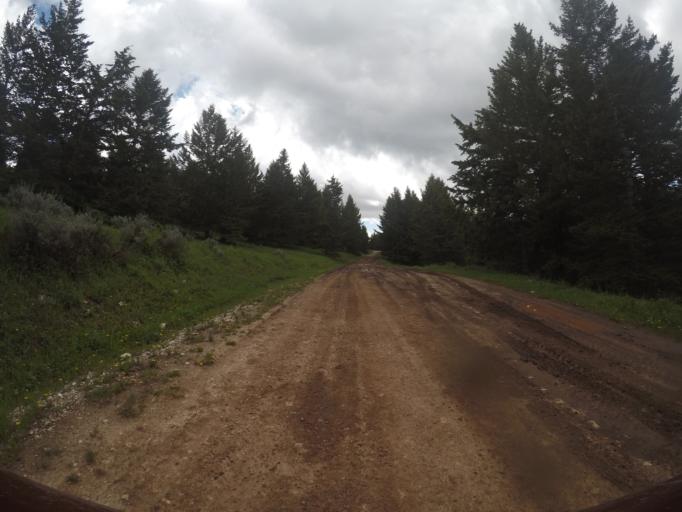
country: US
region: Wyoming
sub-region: Big Horn County
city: Lovell
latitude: 45.1752
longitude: -108.4339
